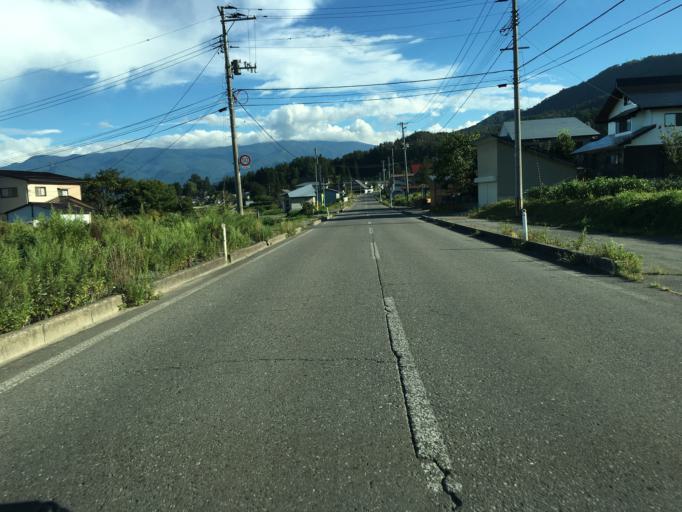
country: JP
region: Yamagata
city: Yonezawa
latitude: 37.9005
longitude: 140.0859
